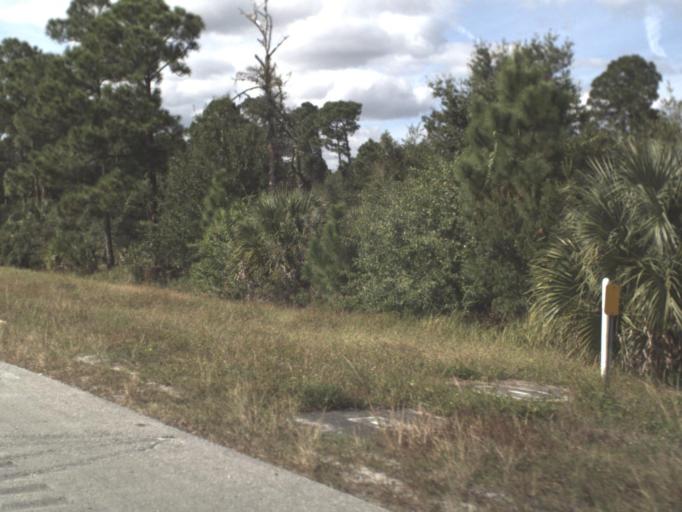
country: US
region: Florida
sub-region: Brevard County
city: Sharpes
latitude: 28.4104
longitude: -80.8017
